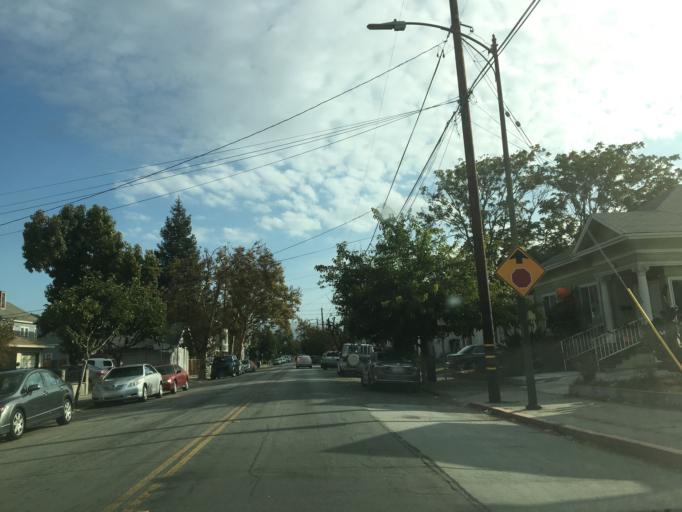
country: US
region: California
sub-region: Santa Clara County
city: San Jose
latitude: 37.3427
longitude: -121.8853
